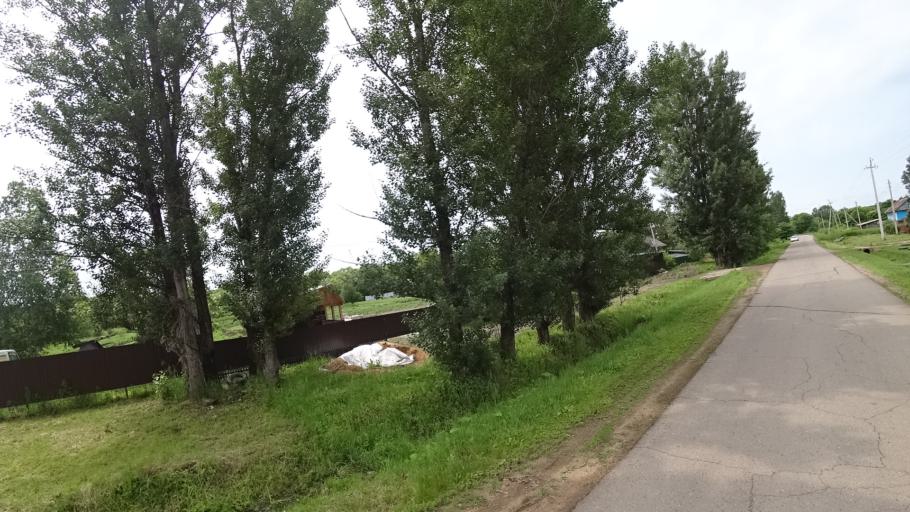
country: RU
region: Primorskiy
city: Novosysoyevka
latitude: 44.2471
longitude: 133.3742
